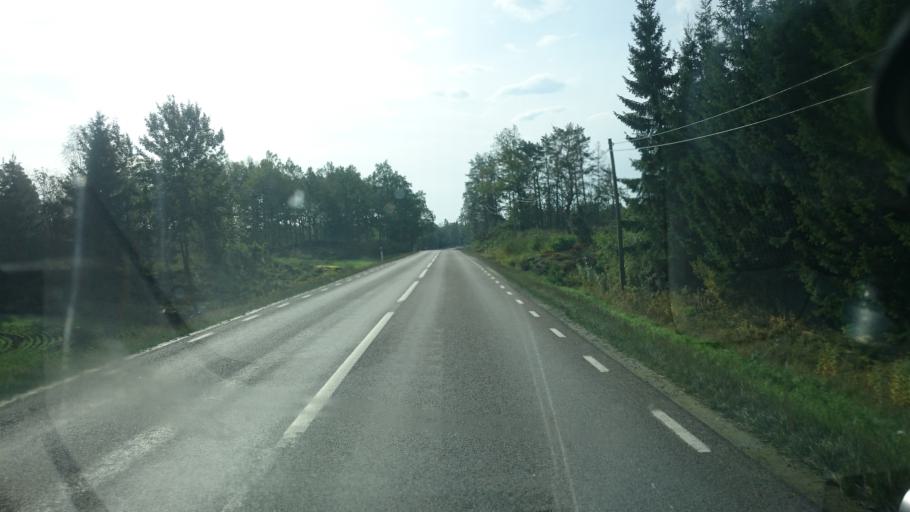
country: SE
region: Vaestra Goetaland
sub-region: Alingsas Kommun
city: Sollebrunn
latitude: 58.2121
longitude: 12.4330
